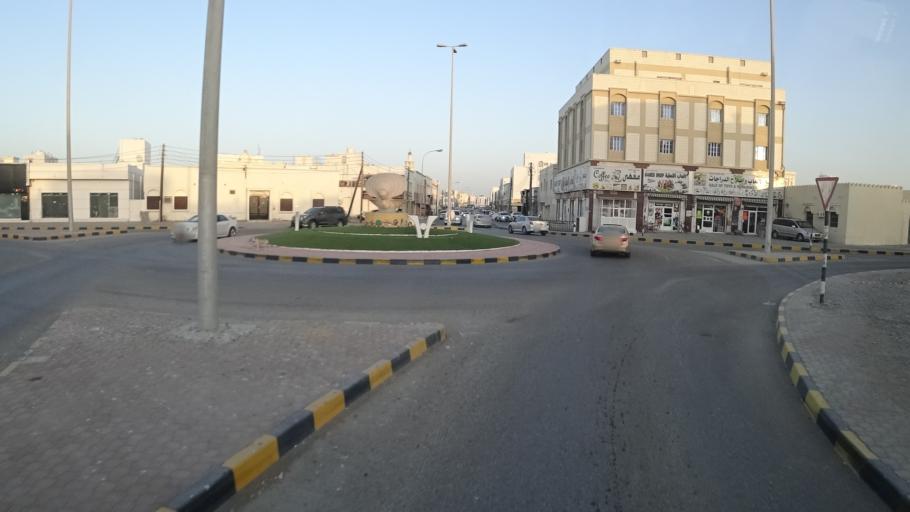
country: OM
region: Ash Sharqiyah
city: Sur
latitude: 22.5814
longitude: 59.5075
